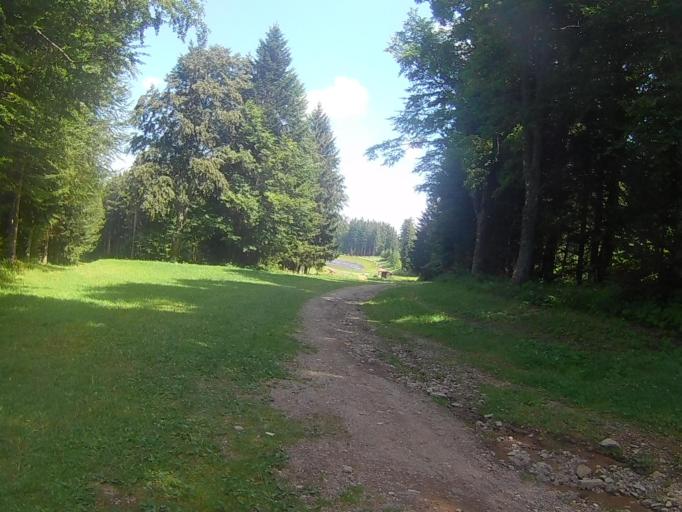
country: SI
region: Ruse
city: Ruse
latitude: 46.4961
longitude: 15.5090
